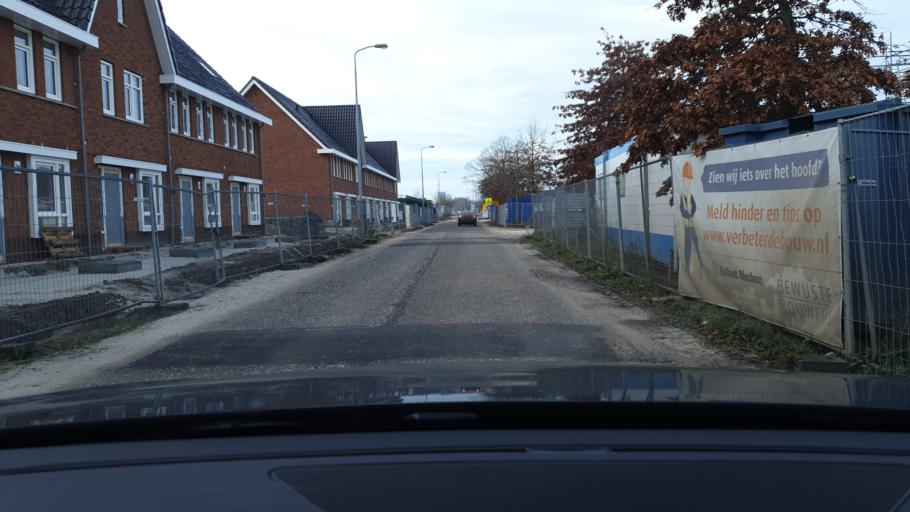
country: NL
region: North Brabant
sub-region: Gemeente Eindhoven
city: Muschberg en Geestenberg
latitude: 51.4348
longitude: 5.5219
